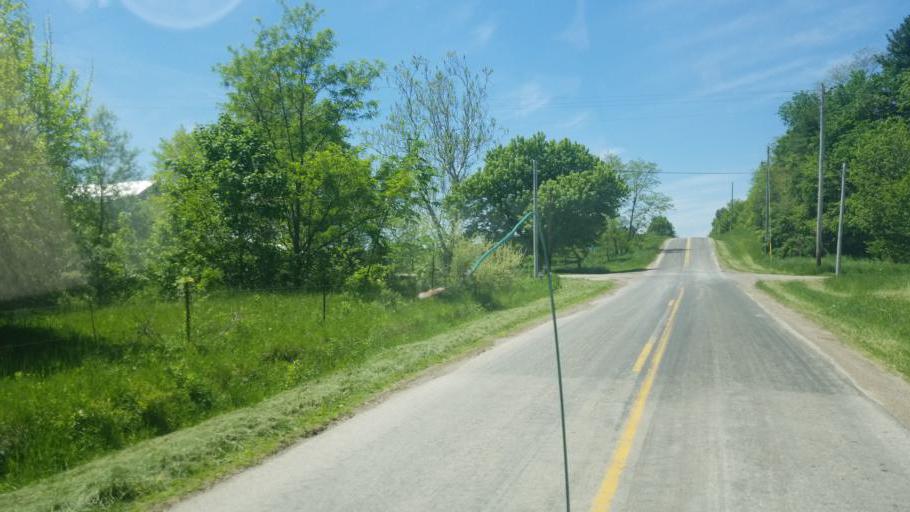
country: US
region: Ohio
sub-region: Huron County
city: New London
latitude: 40.9678
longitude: -82.4070
